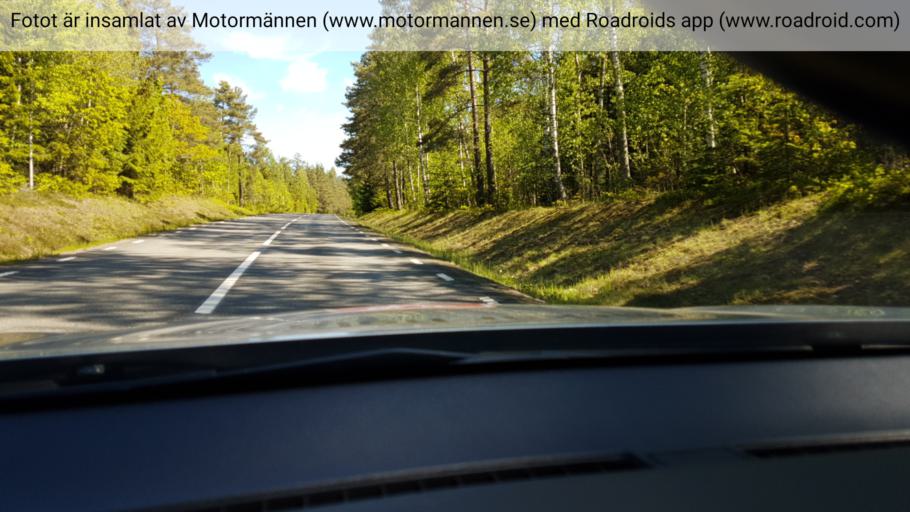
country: SE
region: Vaestra Goetaland
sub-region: Karlsborgs Kommun
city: Molltorp
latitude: 58.4167
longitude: 14.3792
